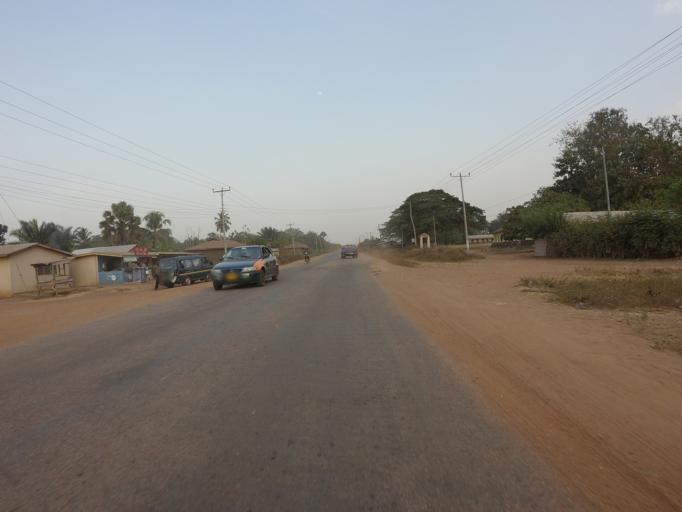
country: GH
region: Volta
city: Ho
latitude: 6.5750
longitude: 0.4159
